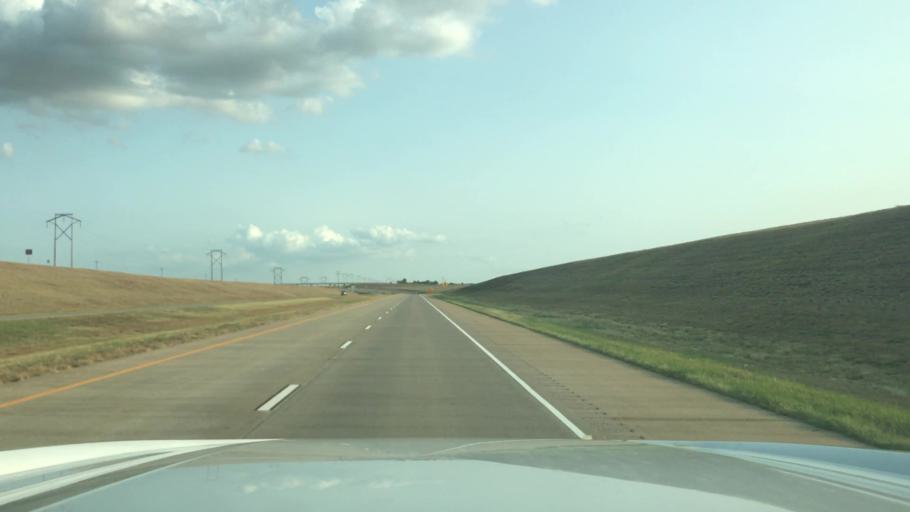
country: US
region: Texas
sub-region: Swisher County
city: Tulia
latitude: 34.5282
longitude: -101.7956
